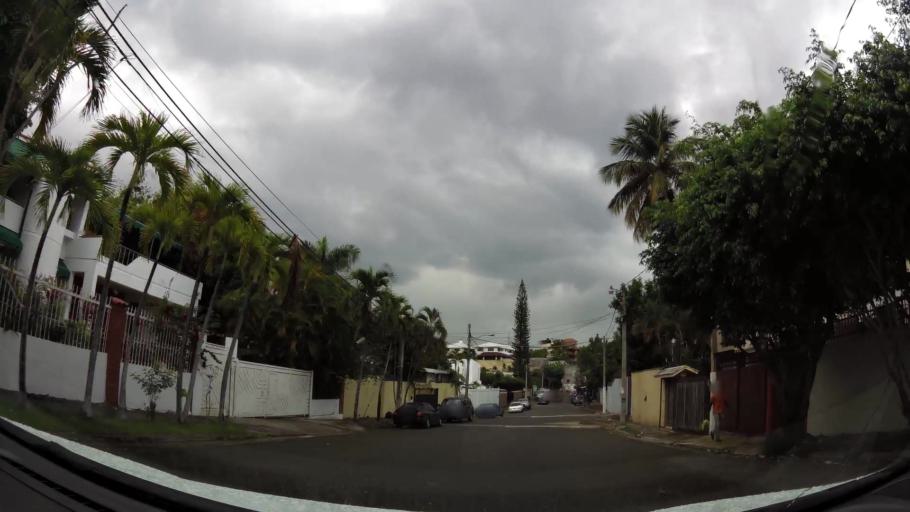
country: DO
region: Nacional
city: La Agustina
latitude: 18.5005
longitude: -69.9391
